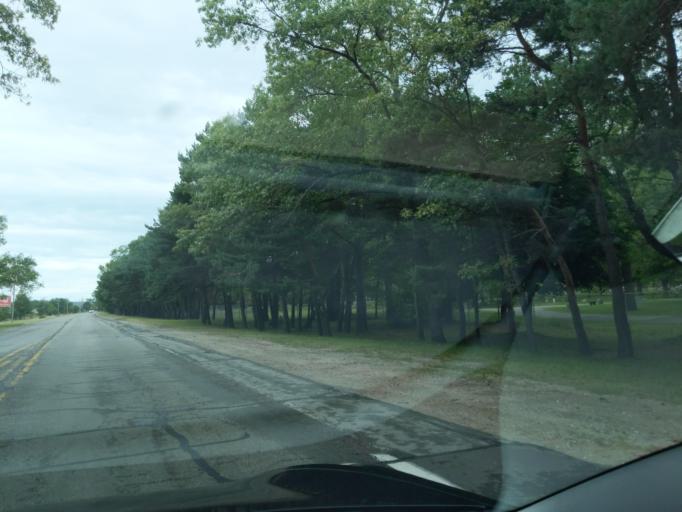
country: US
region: Michigan
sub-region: Grand Traverse County
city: Traverse City
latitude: 44.7523
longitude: -85.5834
